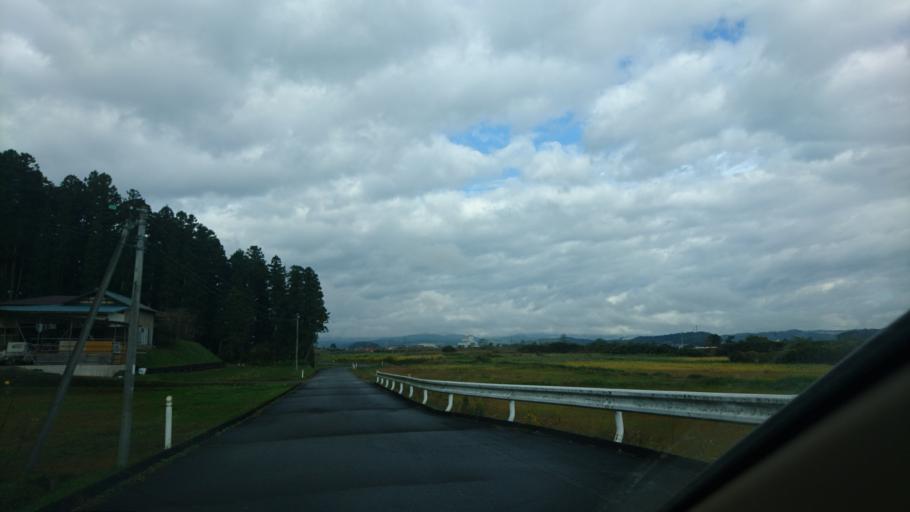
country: JP
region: Iwate
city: Ichinoseki
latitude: 38.7946
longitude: 140.9909
